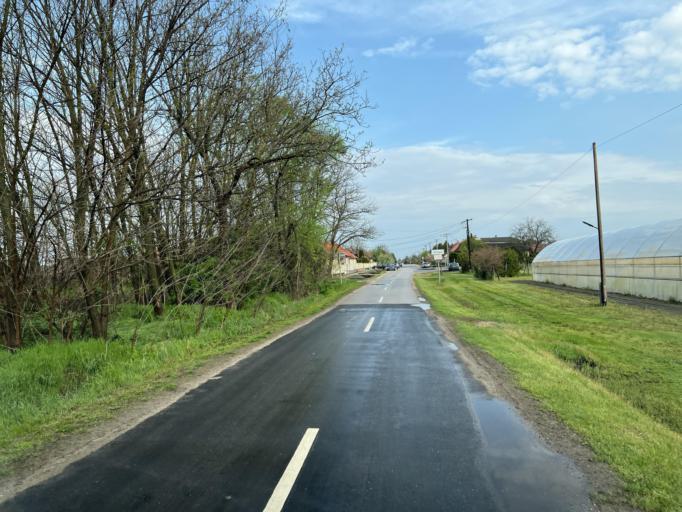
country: HU
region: Pest
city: Nyaregyhaza
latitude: 47.2212
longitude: 19.4596
